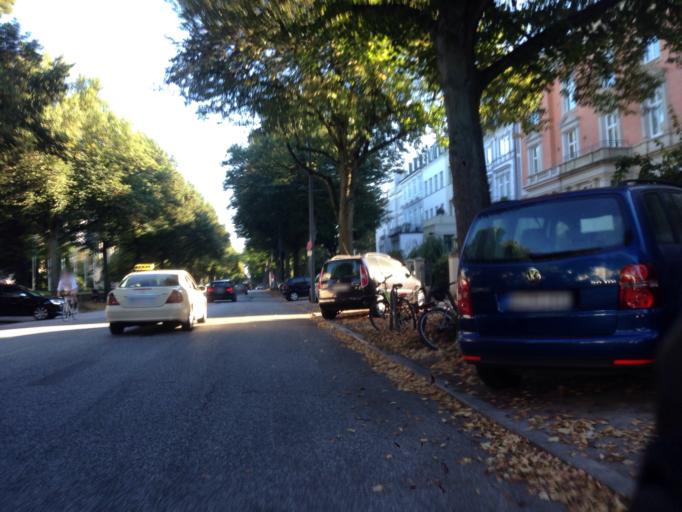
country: DE
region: Hamburg
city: Eimsbuettel
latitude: 53.5769
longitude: 9.9889
